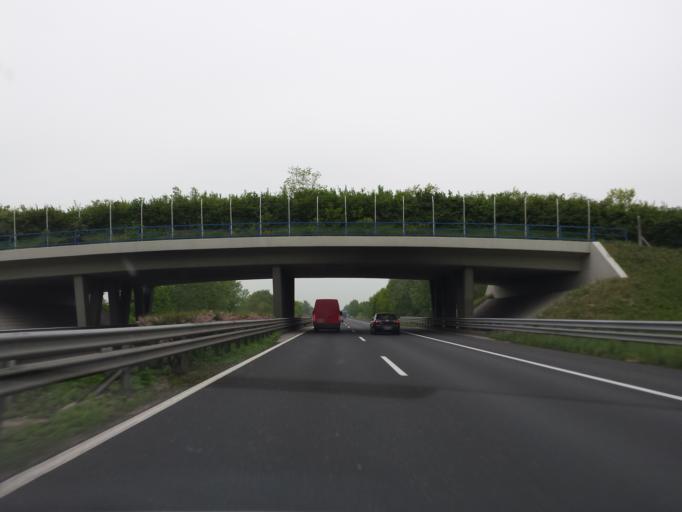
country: HU
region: Gyor-Moson-Sopron
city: Kimle
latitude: 47.7782
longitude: 17.3564
